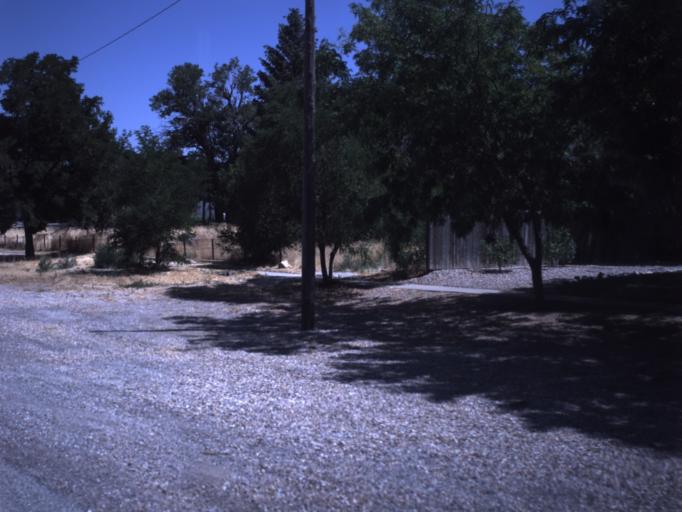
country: US
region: Utah
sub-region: Millard County
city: Delta
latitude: 39.3732
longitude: -112.3361
